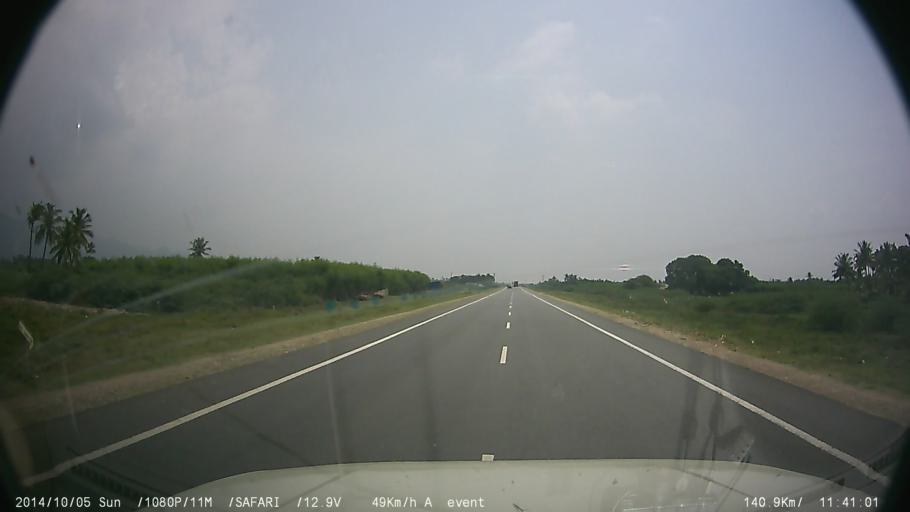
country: IN
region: Tamil Nadu
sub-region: Salem
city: Attur
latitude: 11.6098
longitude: 78.5945
